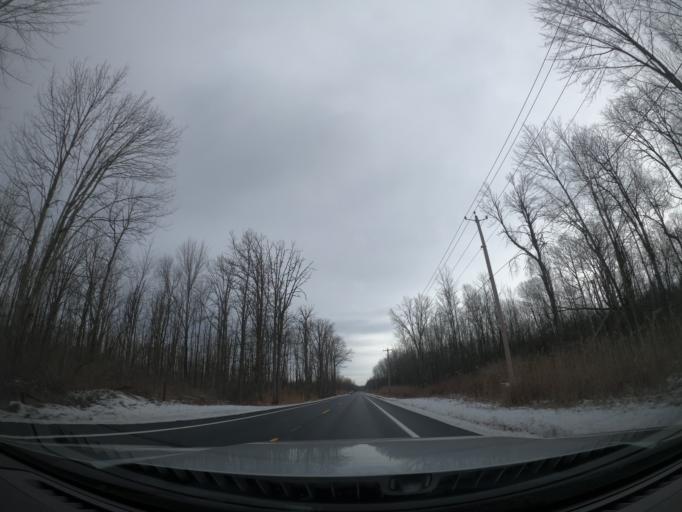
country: US
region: New York
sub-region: Madison County
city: Bridgeport
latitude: 43.1348
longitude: -75.9862
